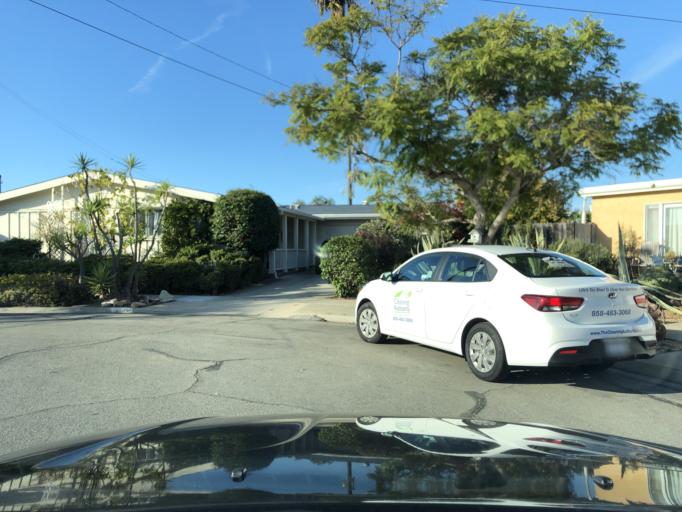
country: US
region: California
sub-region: San Diego County
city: La Jolla
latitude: 32.8258
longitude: -117.1957
